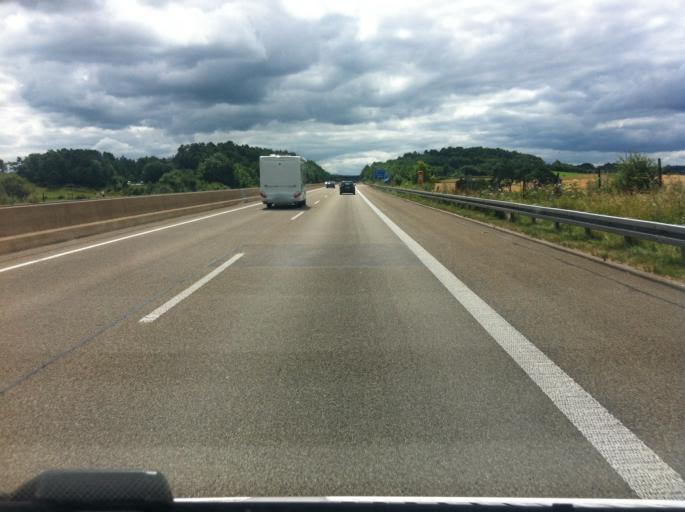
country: DE
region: North Rhine-Westphalia
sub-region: Regierungsbezirk Koln
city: Nettersheim
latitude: 50.5323
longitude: 6.6728
